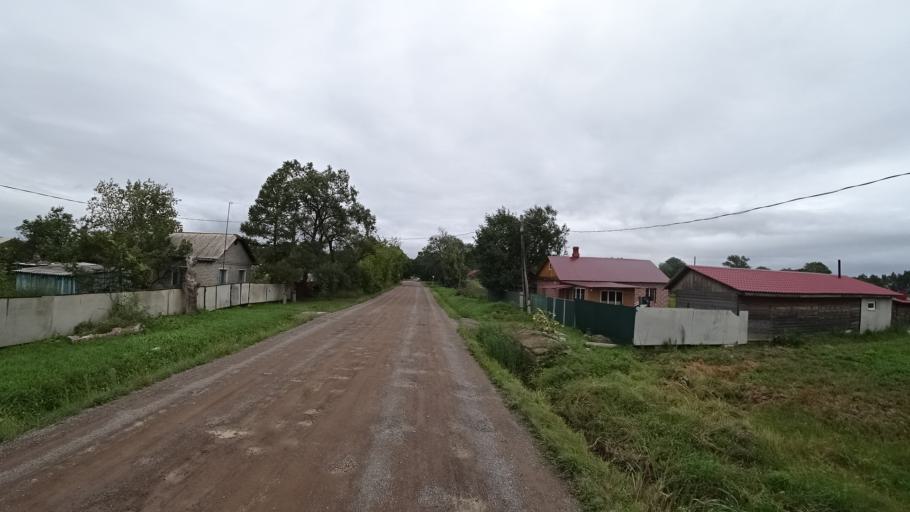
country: RU
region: Primorskiy
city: Chernigovka
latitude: 44.3405
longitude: 132.5683
